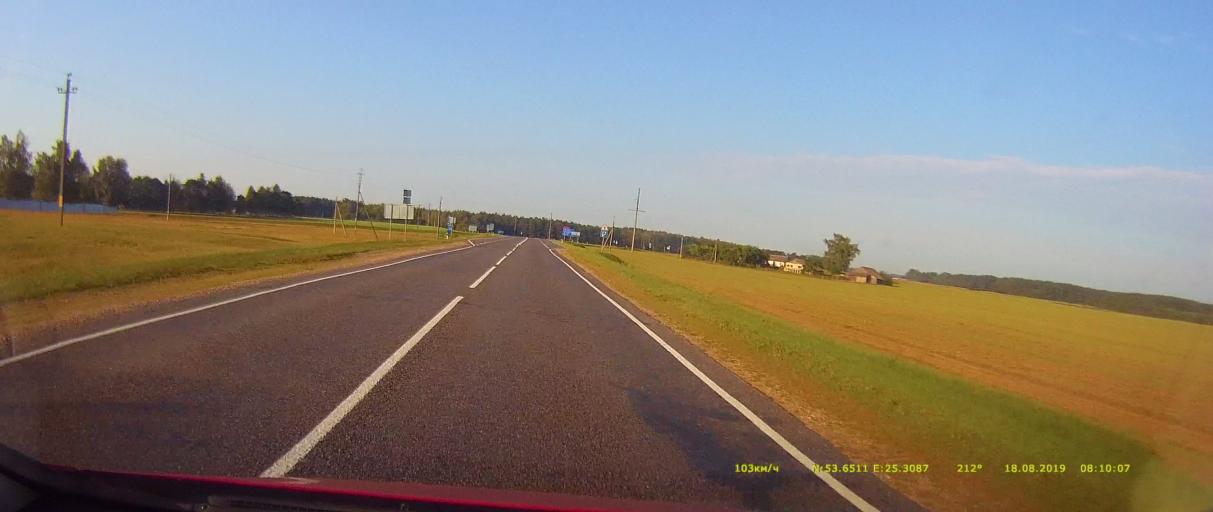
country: BY
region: Grodnenskaya
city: Dzyatlava
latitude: 53.6273
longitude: 25.3234
